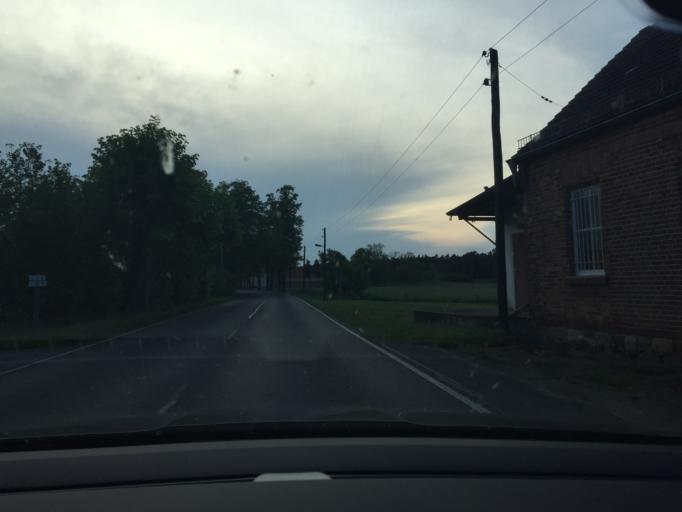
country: DE
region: Brandenburg
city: Beelitz
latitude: 52.1395
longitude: 12.9841
